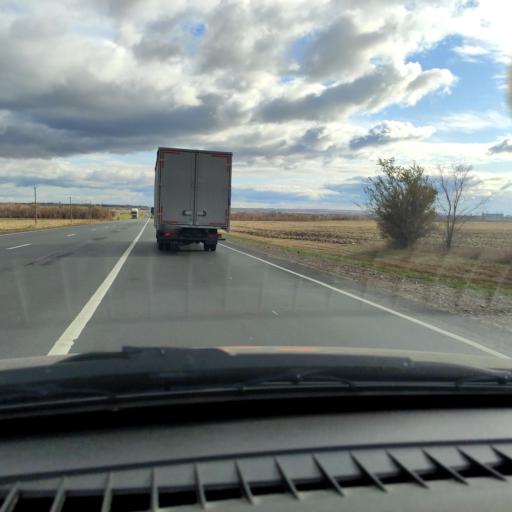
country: RU
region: Samara
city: Varlamovo
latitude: 53.2113
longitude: 48.4615
